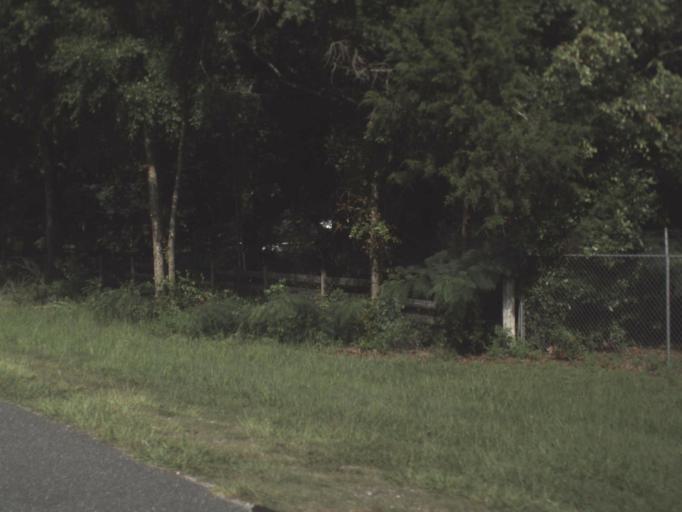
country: US
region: Florida
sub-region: Suwannee County
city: Wellborn
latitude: 30.0334
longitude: -82.8213
